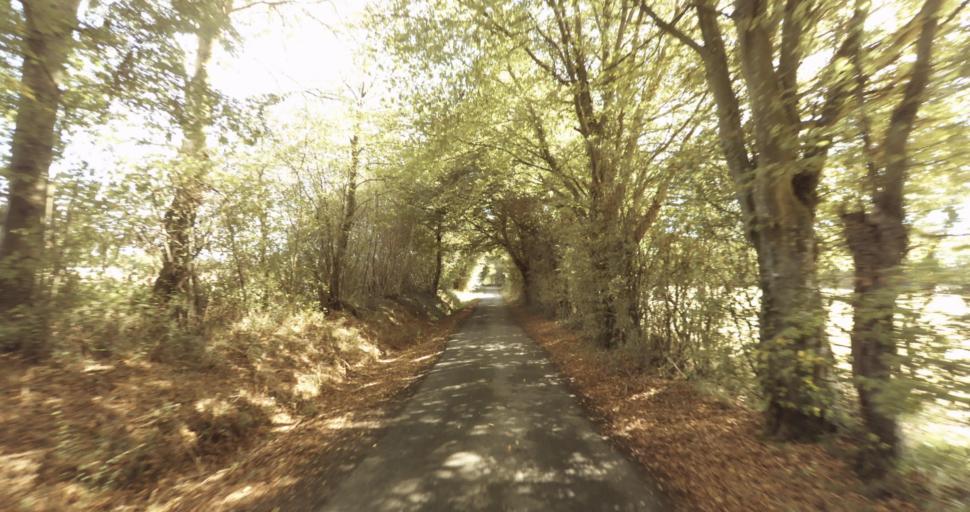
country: FR
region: Lower Normandy
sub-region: Departement de l'Orne
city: Vimoutiers
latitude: 48.9341
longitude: 0.2508
